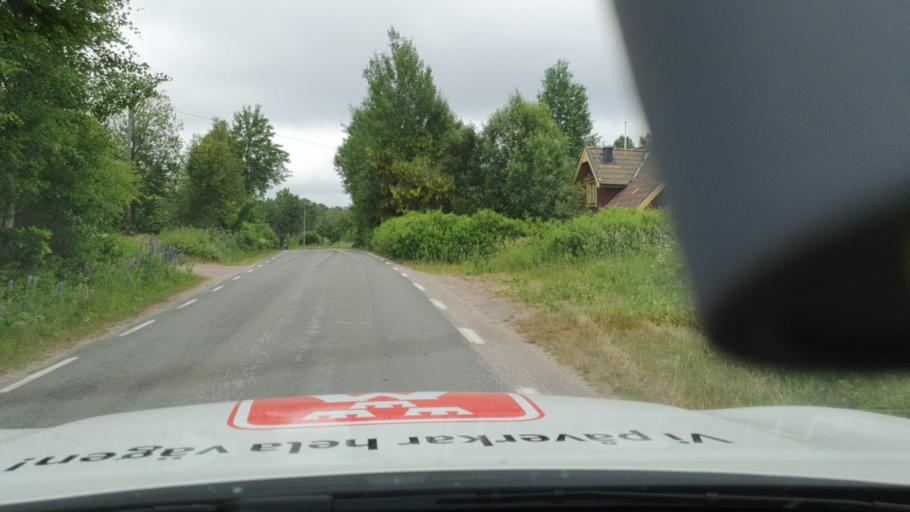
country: SE
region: Vaestra Goetaland
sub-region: Tibro Kommun
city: Tibro
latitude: 58.3573
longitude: 14.1989
